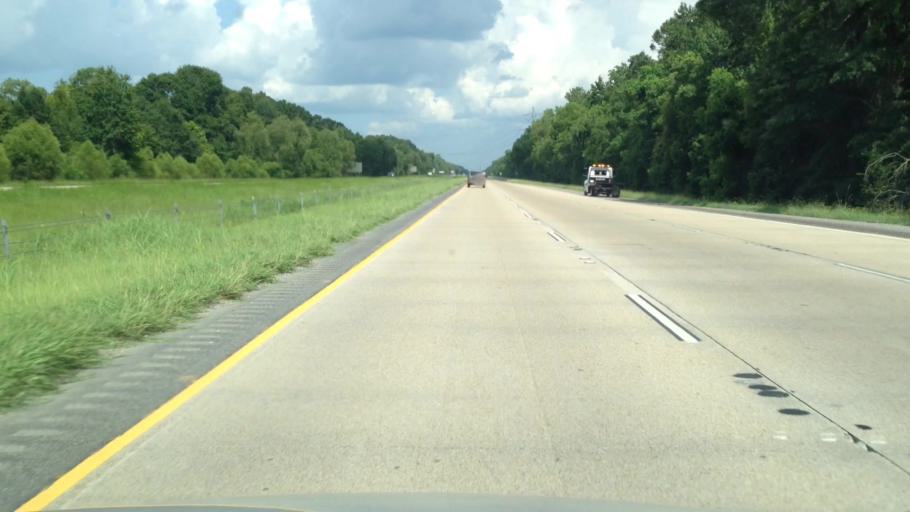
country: US
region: Louisiana
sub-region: Ascension Parish
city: Sorrento
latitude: 30.1697
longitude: -90.8710
